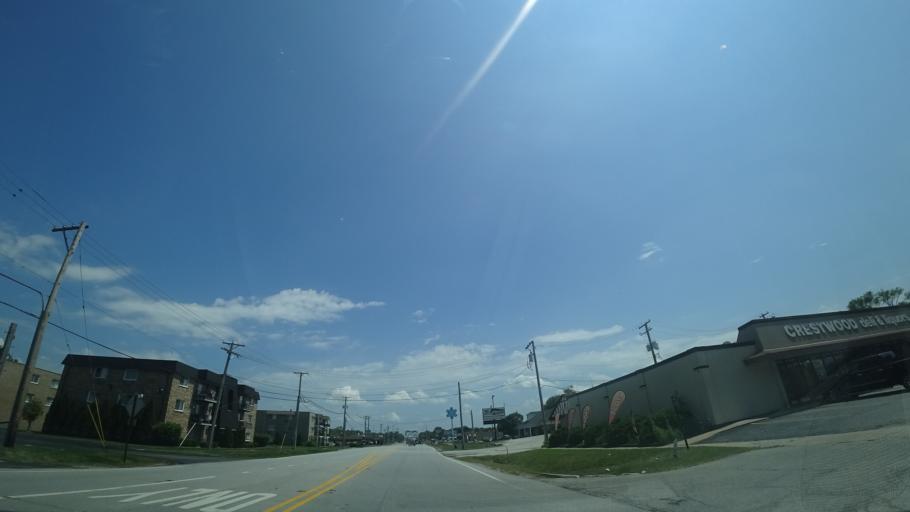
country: US
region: Illinois
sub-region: Cook County
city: Crestwood
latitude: 41.6614
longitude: -87.7574
